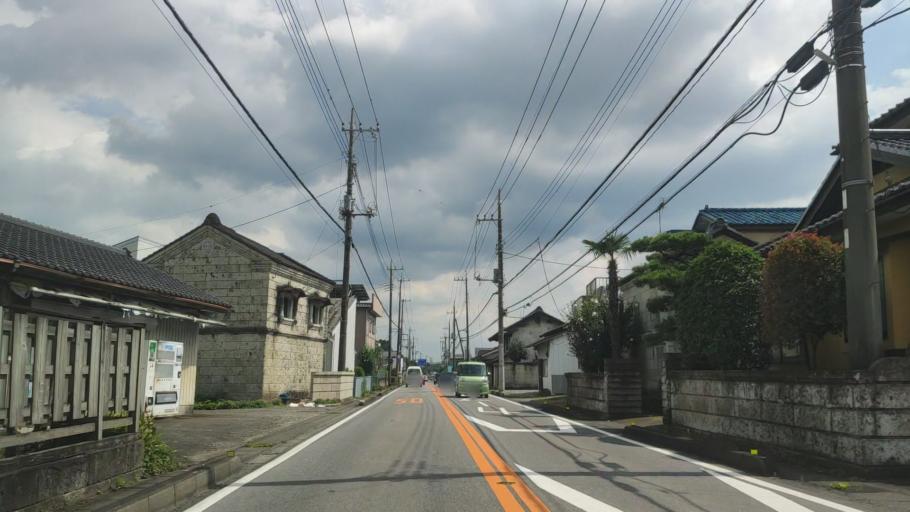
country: JP
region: Tochigi
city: Utsunomiya-shi
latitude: 36.6526
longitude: 139.8422
